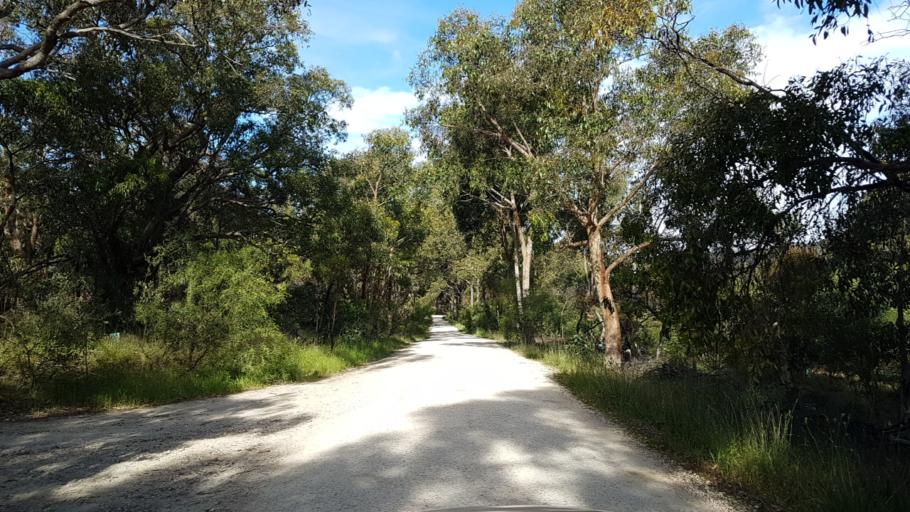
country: AU
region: South Australia
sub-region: Adelaide Hills
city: Adelaide Hills
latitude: -34.9049
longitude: 138.7434
